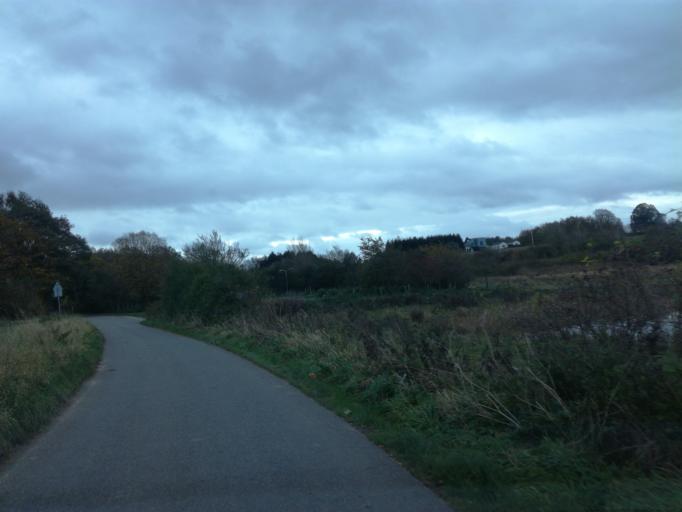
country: DK
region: South Denmark
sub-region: Fredericia Kommune
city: Fredericia
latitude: 55.6202
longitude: 9.7492
